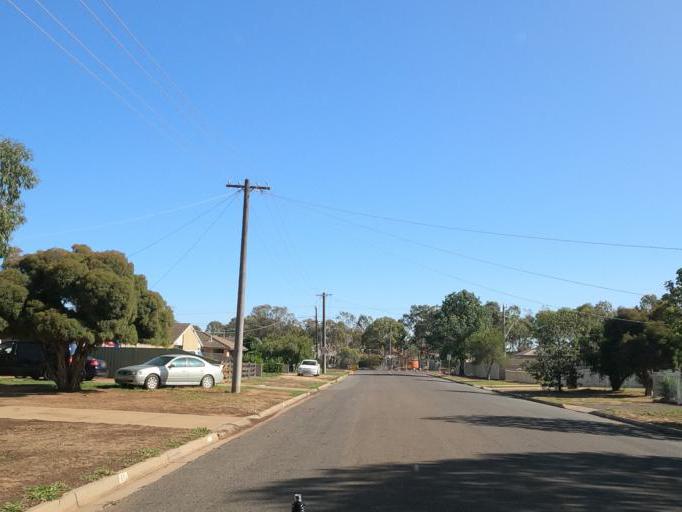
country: AU
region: Victoria
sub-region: Moira
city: Yarrawonga
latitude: -36.0230
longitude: 146.0087
